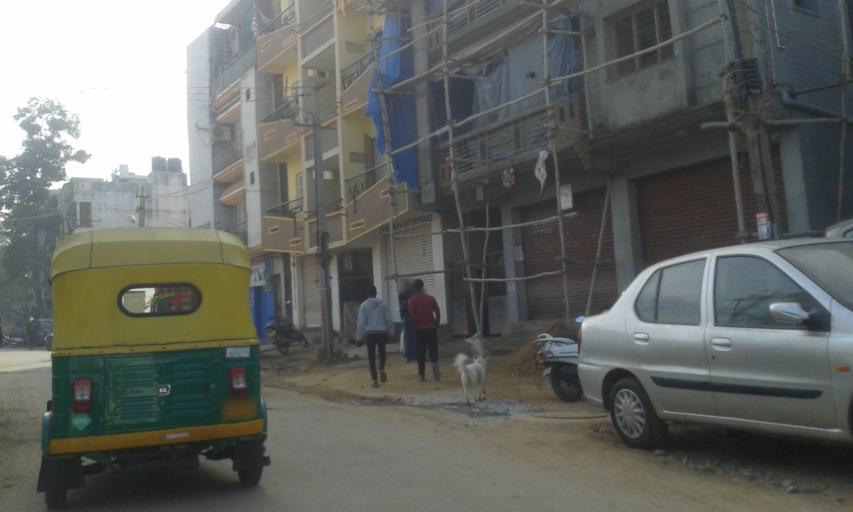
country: IN
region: Karnataka
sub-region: Bangalore Urban
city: Bangalore
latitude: 12.9566
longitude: 77.6193
